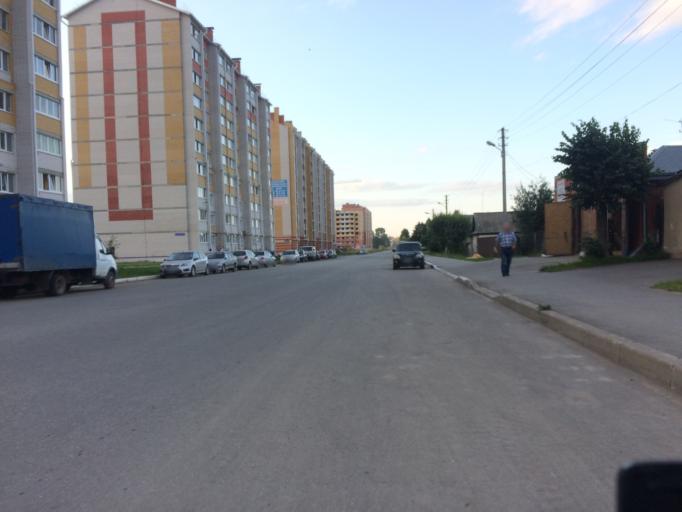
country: RU
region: Mariy-El
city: Medvedevo
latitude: 56.6469
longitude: 47.8354
